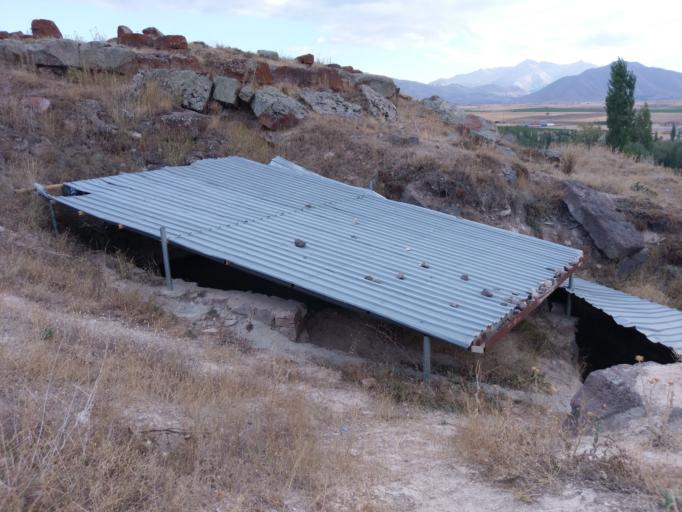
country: TR
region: Kayseri
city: Toklar
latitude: 38.4640
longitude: 36.0794
